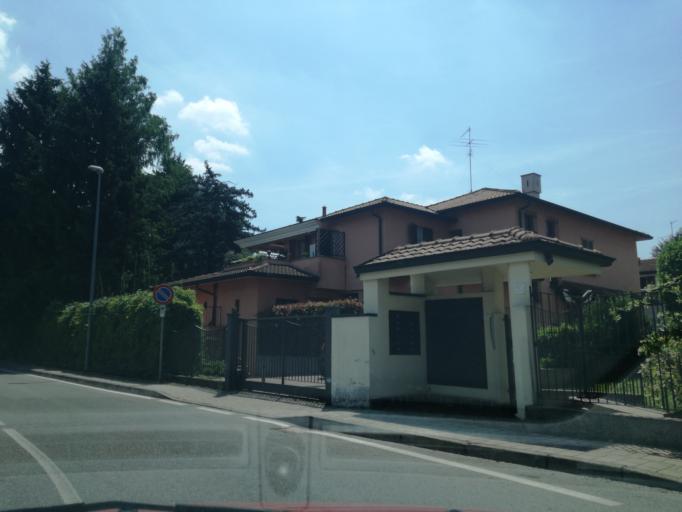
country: IT
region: Lombardy
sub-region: Provincia di Monza e Brianza
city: Biassono
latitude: 45.6291
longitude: 9.2651
